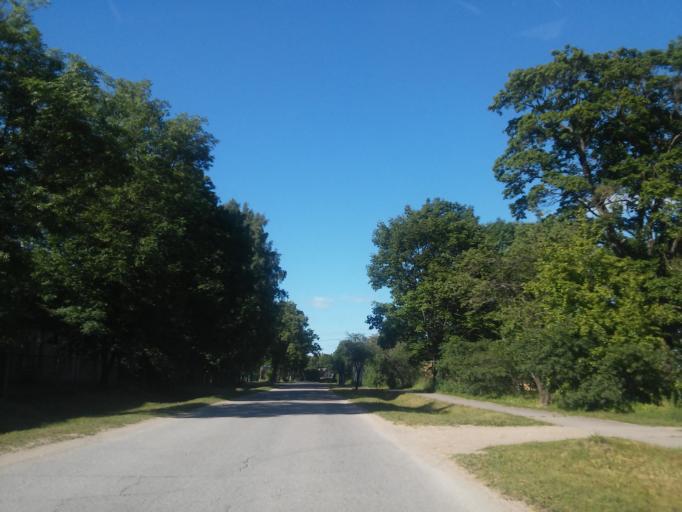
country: LV
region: Vainode
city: Vainode
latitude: 56.4311
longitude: 21.8707
